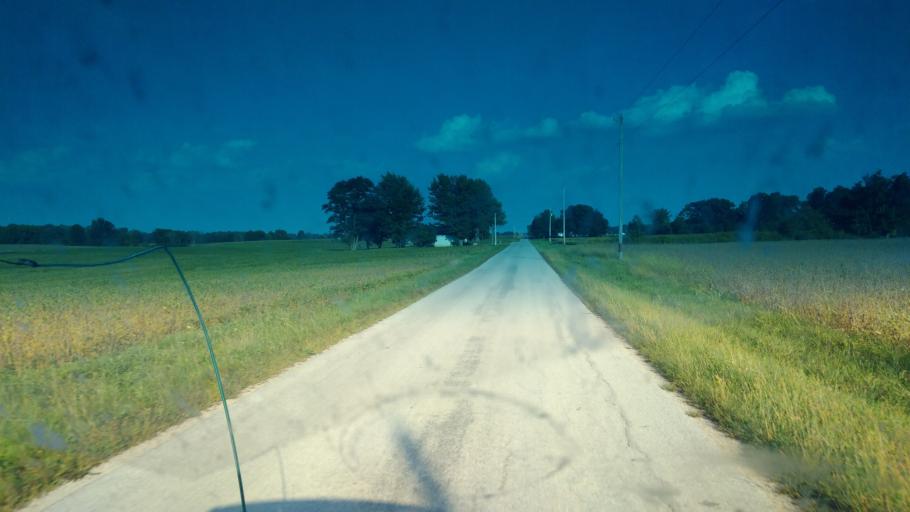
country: US
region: Ohio
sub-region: Wyandot County
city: Upper Sandusky
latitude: 40.9352
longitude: -83.1855
